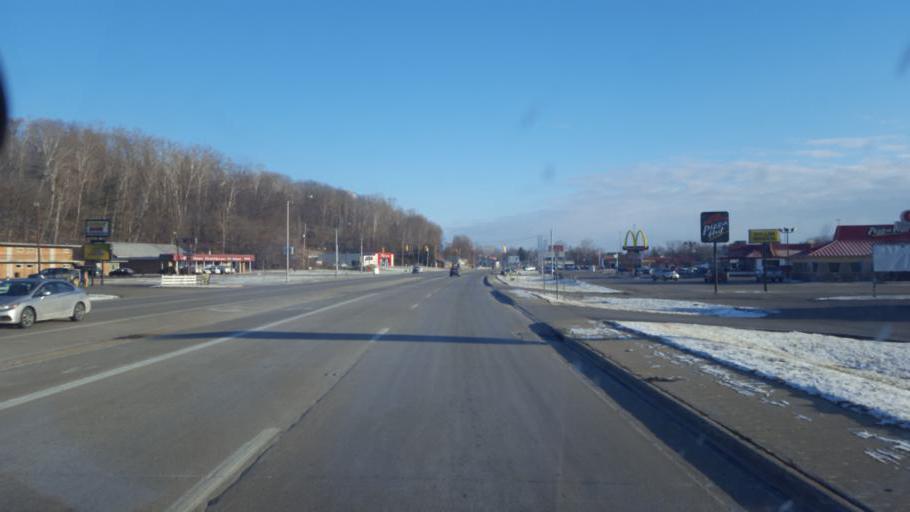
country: US
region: Ohio
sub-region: Pike County
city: Waverly
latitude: 39.1193
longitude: -82.9943
